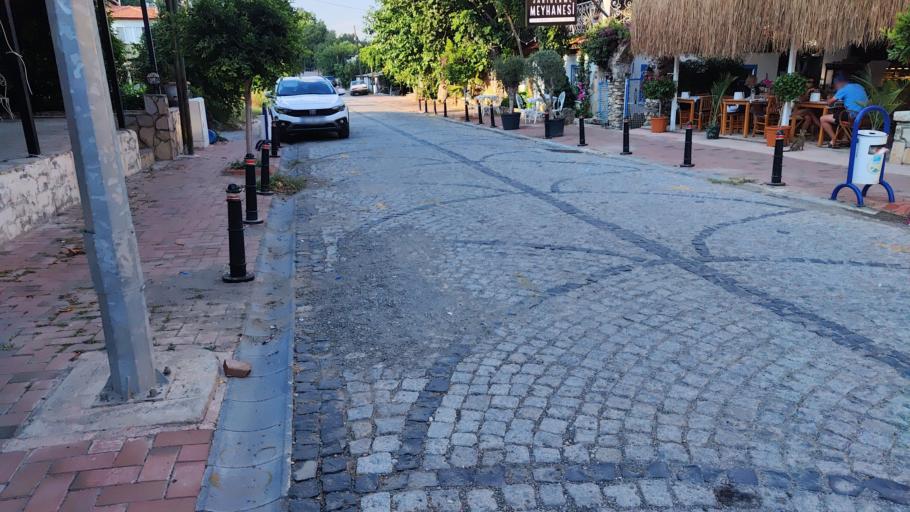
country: TR
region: Mugla
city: Sarigerme
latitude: 36.7147
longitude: 28.7046
